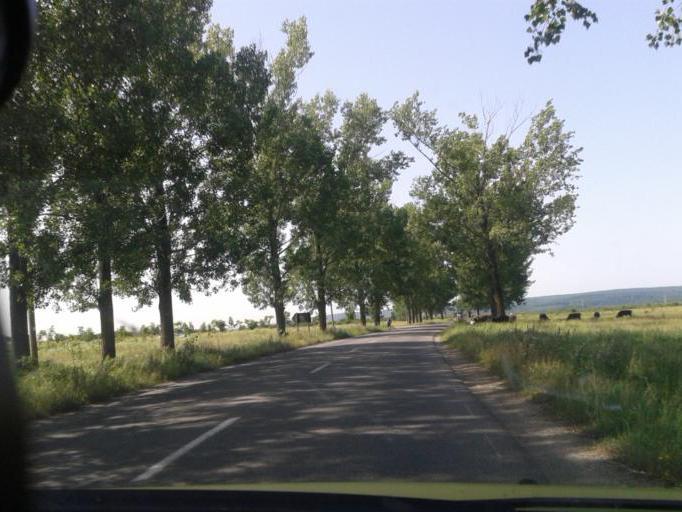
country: RO
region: Prahova
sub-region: Comuna Dumbravesti
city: Dumbravesti
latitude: 45.0768
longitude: 25.9933
